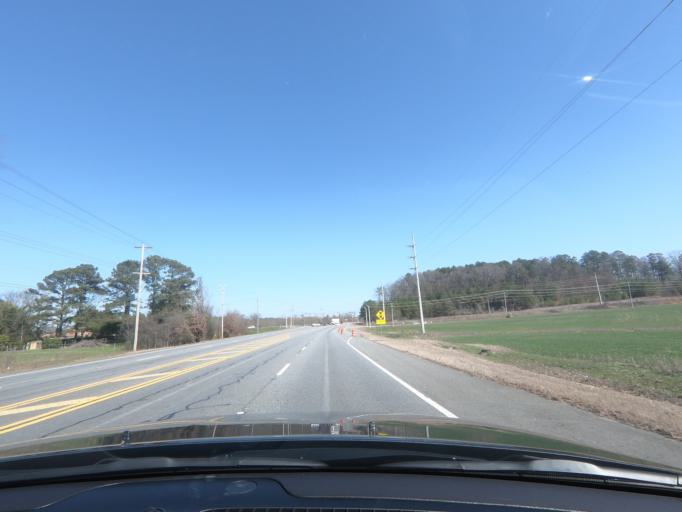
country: US
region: Georgia
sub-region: Gordon County
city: Calhoun
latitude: 34.4777
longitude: -84.9606
